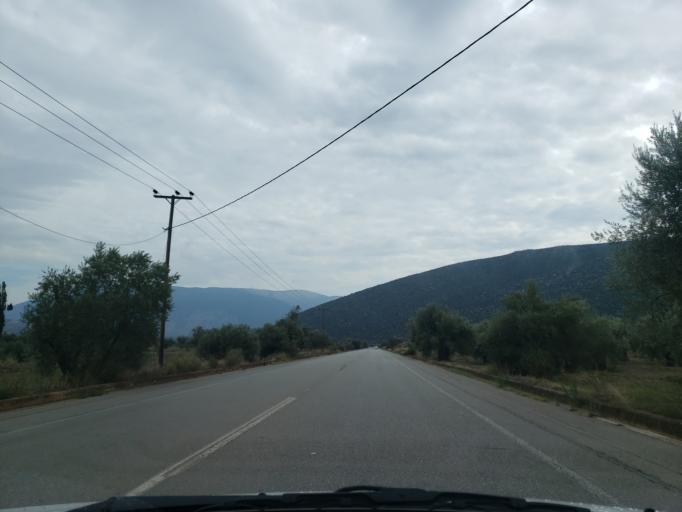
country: GR
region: Central Greece
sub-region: Nomos Fokidos
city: Amfissa
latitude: 38.4897
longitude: 22.4172
